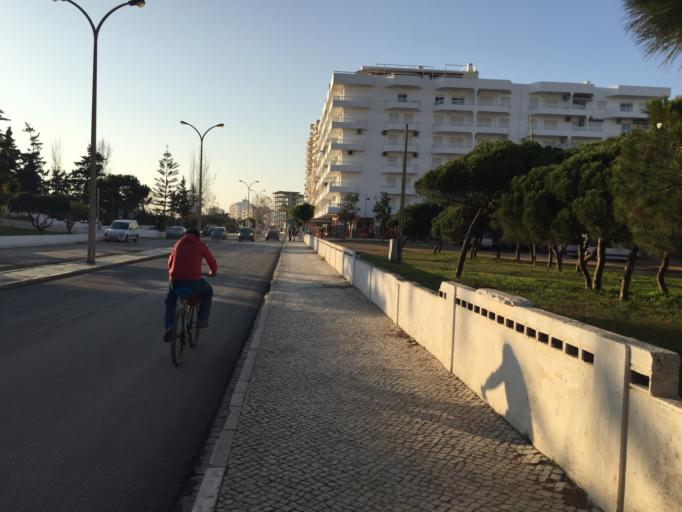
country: PT
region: Faro
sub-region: Vila Real de Santo Antonio
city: Monte Gordo
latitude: 37.1793
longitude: -7.4461
